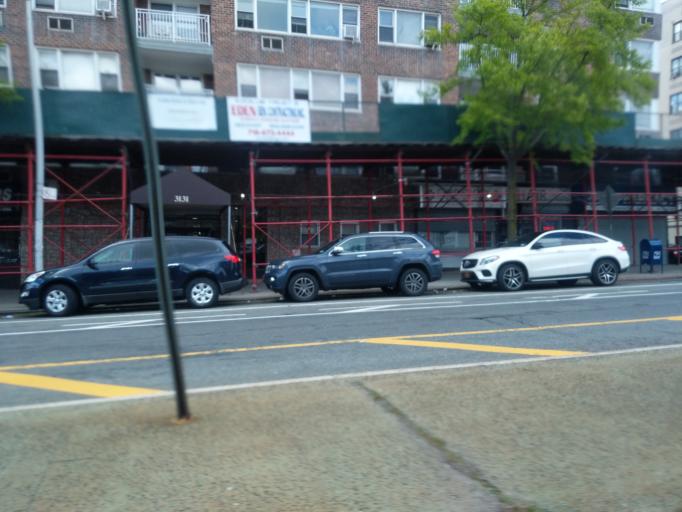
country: US
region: New York
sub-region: Bronx
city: The Bronx
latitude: 40.8752
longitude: -73.8864
